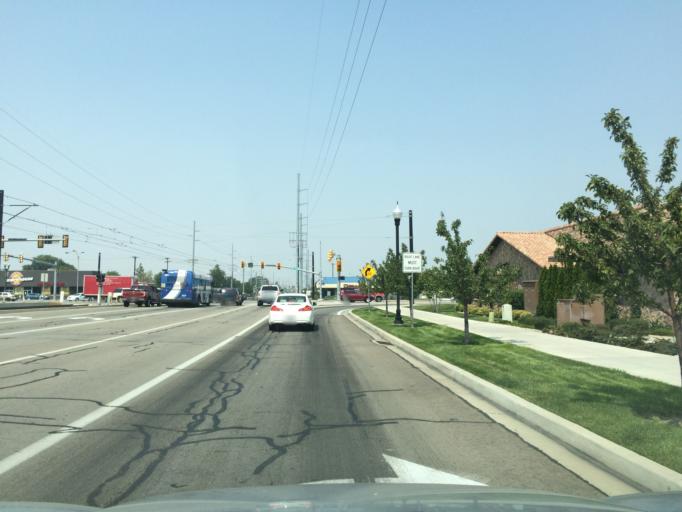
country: US
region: Utah
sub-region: Salt Lake County
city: Taylorsville
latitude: 40.6958
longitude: -111.9579
